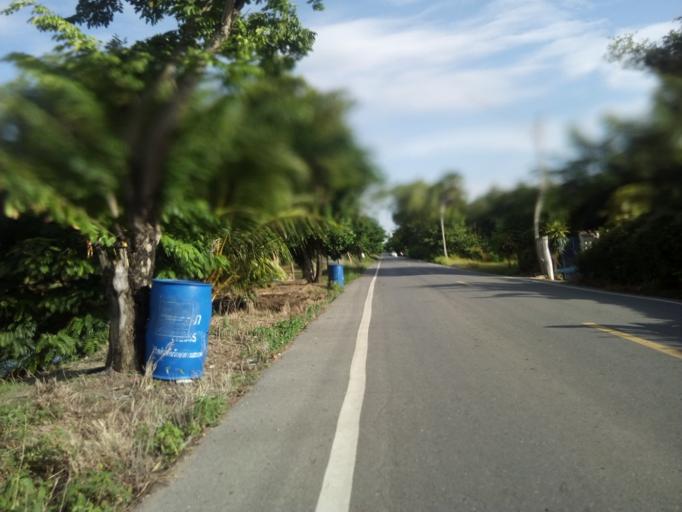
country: TH
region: Pathum Thani
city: Nong Suea
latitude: 14.1246
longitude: 100.8461
